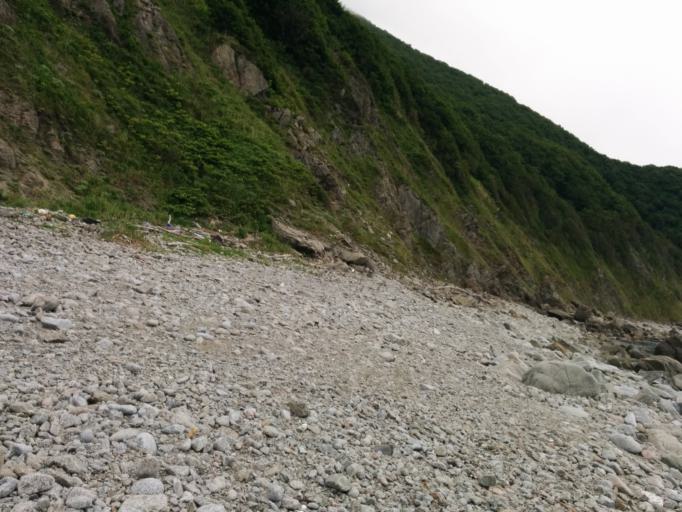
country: JP
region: Hokkaido
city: Iwanai
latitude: 42.3102
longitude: 139.7671
